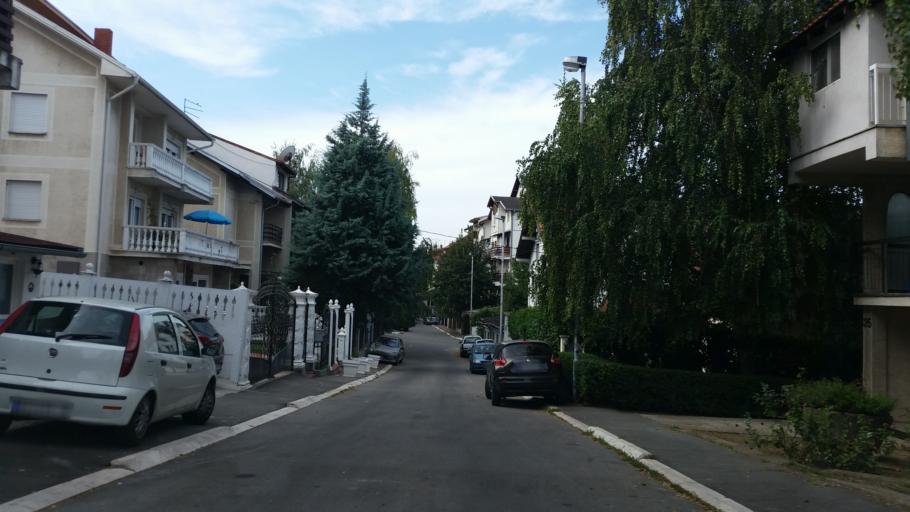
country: RS
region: Central Serbia
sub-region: Belgrade
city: Palilula
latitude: 44.8291
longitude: 20.5499
